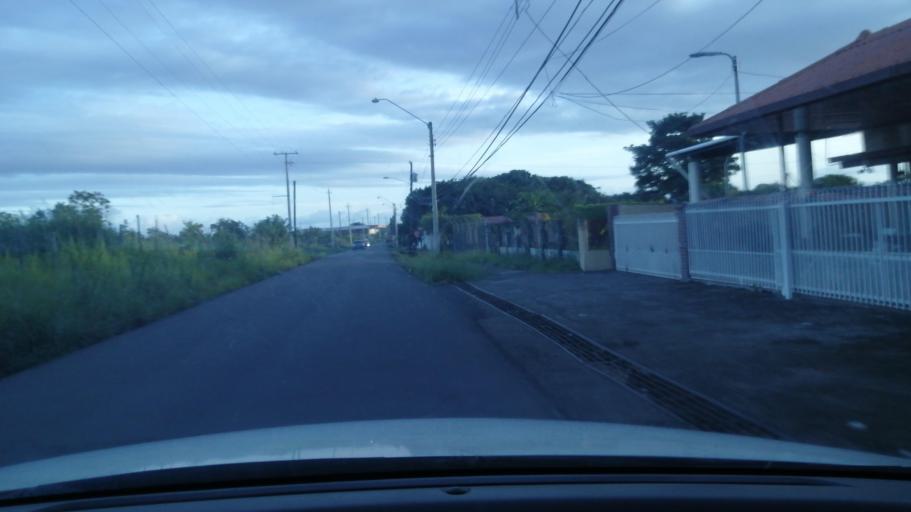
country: PA
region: Chiriqui
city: David
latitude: 8.4047
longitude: -82.4347
